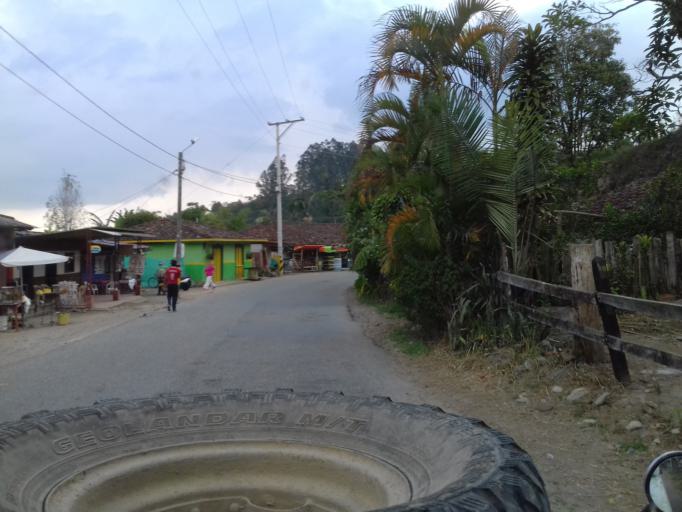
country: CO
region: Quindio
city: Salento
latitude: 4.6428
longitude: -75.5851
